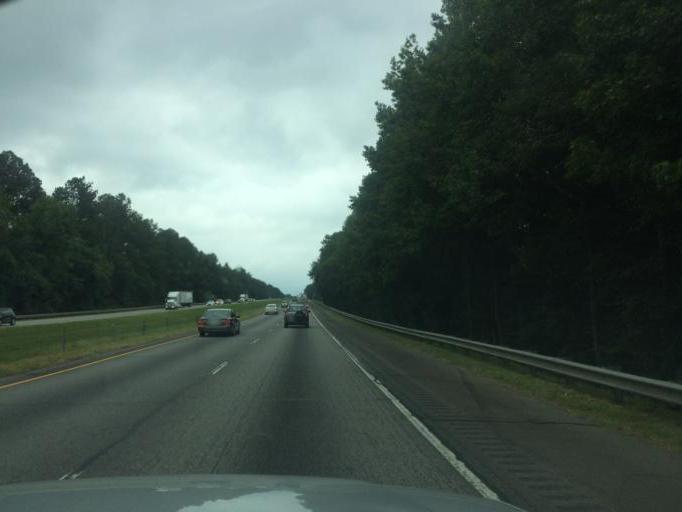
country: US
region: Georgia
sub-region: Franklin County
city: Carnesville
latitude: 34.3993
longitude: -83.2115
